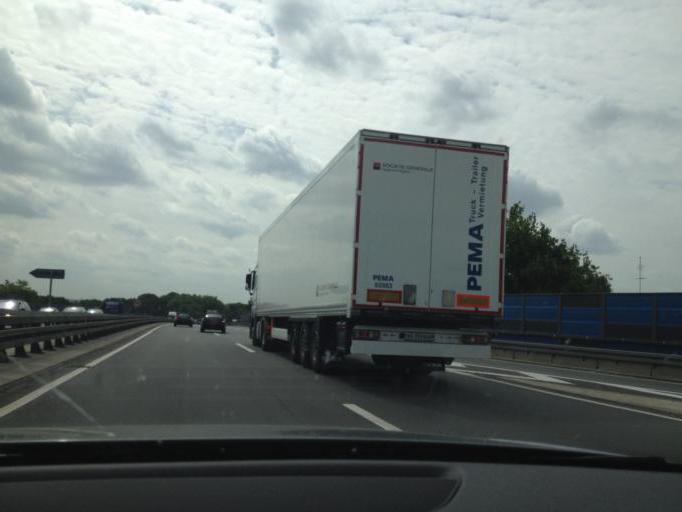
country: DE
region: North Rhine-Westphalia
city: Meiderich
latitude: 51.4686
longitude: 6.7664
